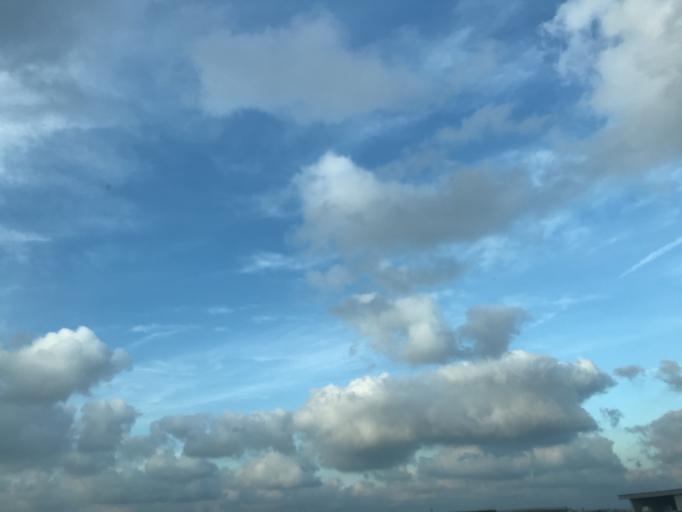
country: TR
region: Istanbul
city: Durusu
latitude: 41.2583
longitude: 28.7122
